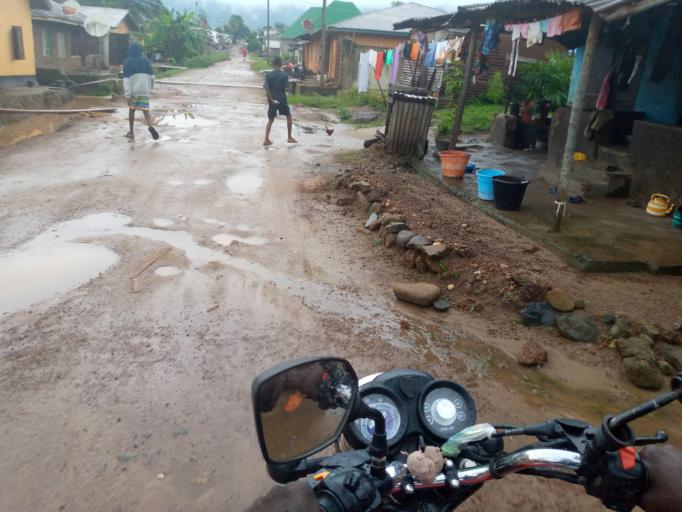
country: SL
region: Eastern Province
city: Kenema
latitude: 7.8834
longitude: -11.1817
